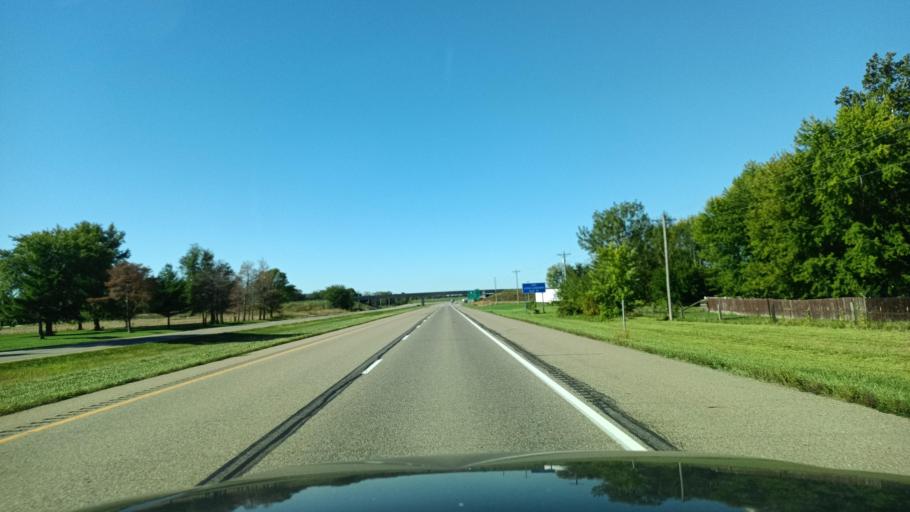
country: US
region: Iowa
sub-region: Lee County
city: Fort Madison
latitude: 40.6755
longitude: -91.2605
